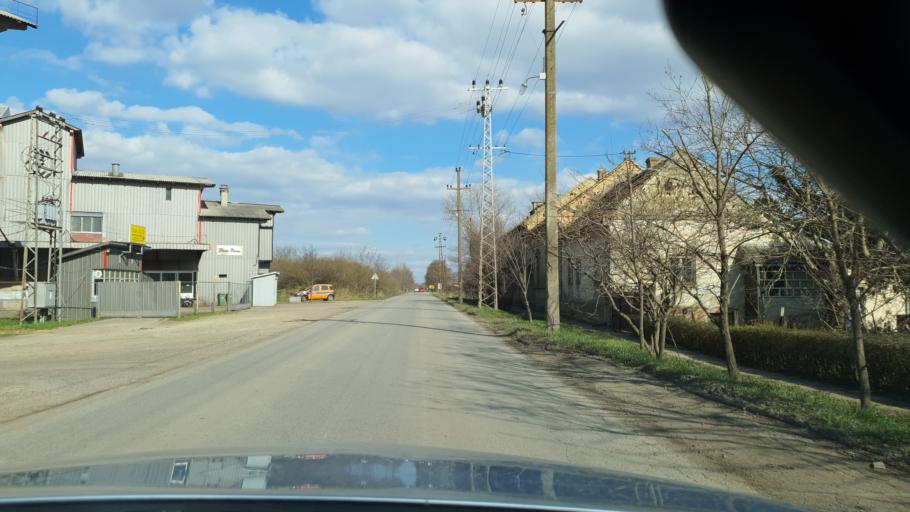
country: RS
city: Ravno Selo
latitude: 45.4521
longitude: 19.6341
